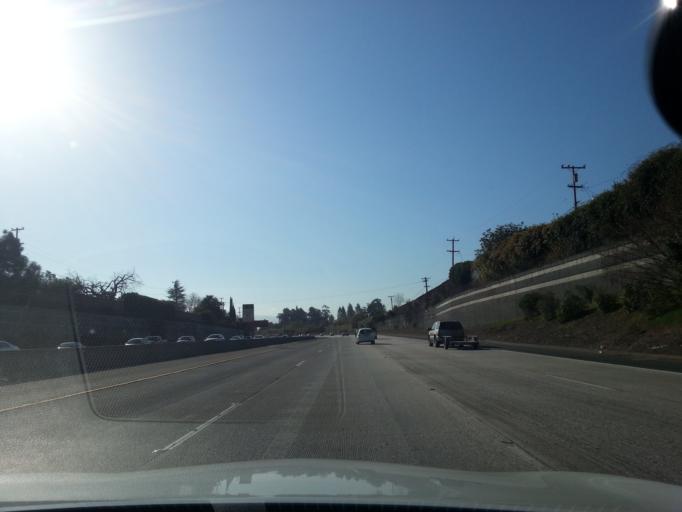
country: US
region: California
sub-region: Santa Clara County
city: Cupertino
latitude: 37.3144
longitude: -122.0463
